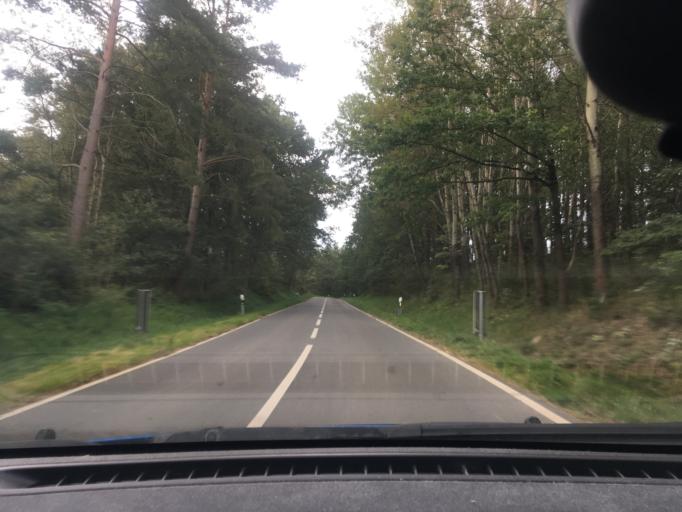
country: DE
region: Lower Saxony
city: Nahrendorf
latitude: 53.1660
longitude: 10.8353
